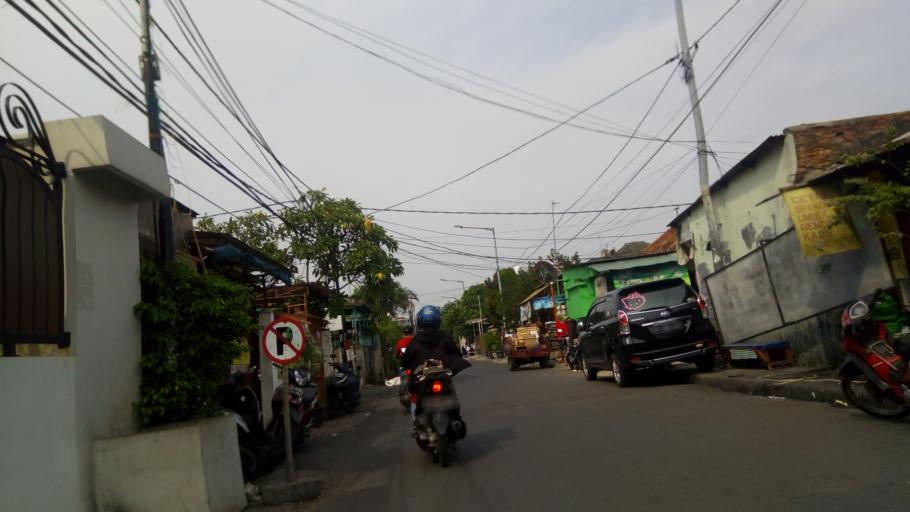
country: ID
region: Jakarta Raya
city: Jakarta
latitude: -6.1718
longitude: 106.8501
